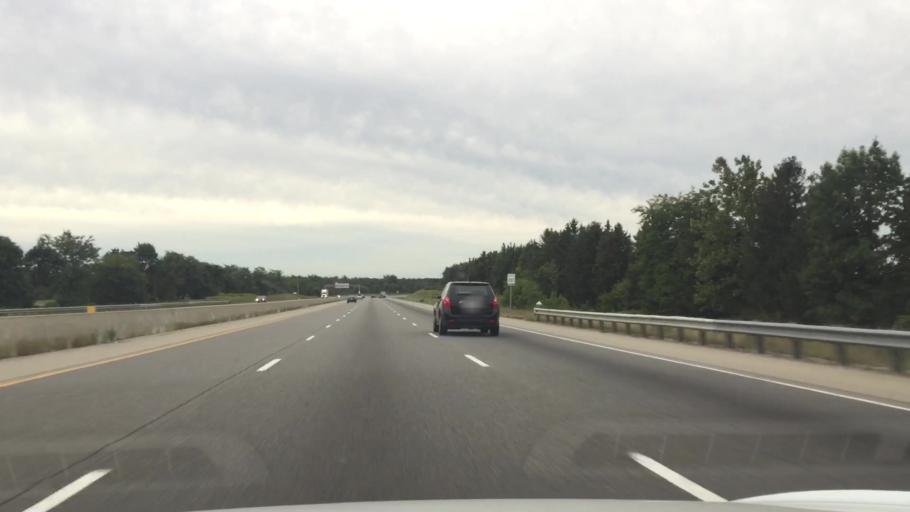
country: CA
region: Ontario
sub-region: Oxford County
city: Woodstock
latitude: 43.2215
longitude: -80.6044
